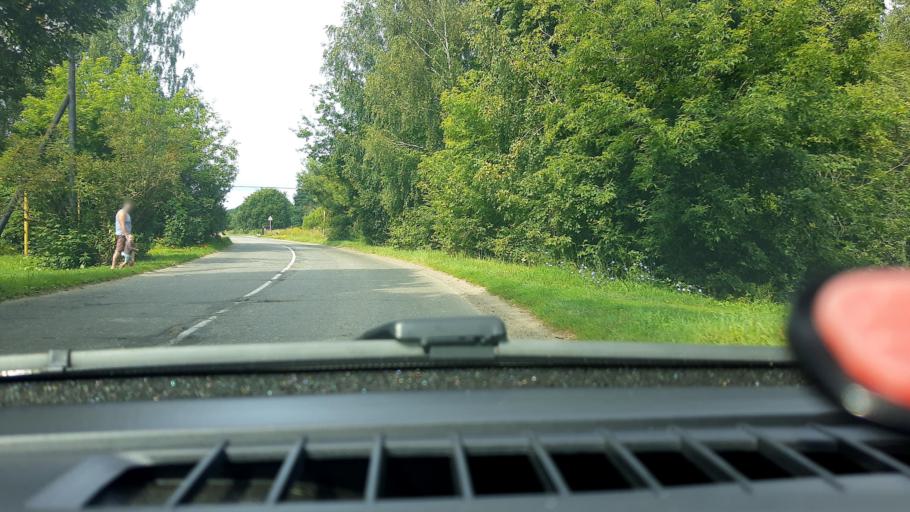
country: RU
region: Nizjnij Novgorod
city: Bogorodsk
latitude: 56.0677
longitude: 43.6578
